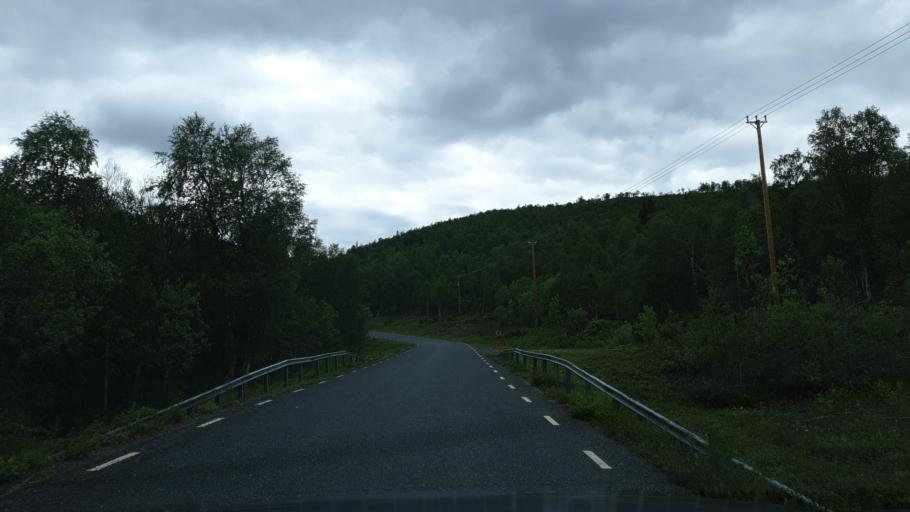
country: NO
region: Nordland
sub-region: Hattfjelldal
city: Hattfjelldal
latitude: 65.4170
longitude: 14.7398
